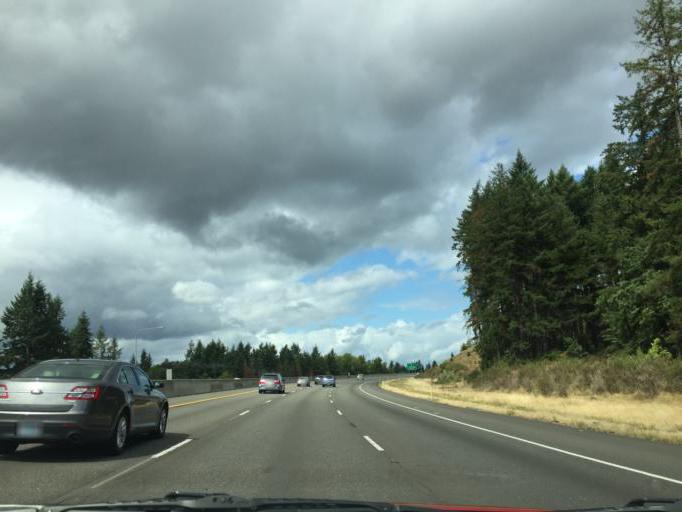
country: US
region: Washington
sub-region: Thurston County
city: Grand Mound
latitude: 46.7928
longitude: -123.0095
